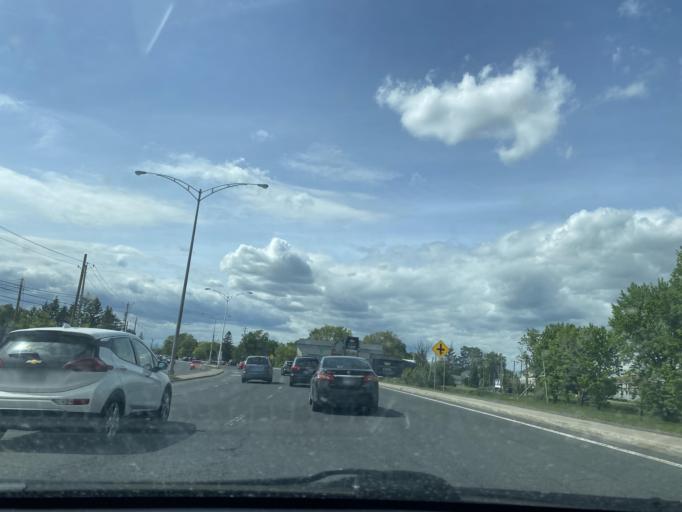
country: CA
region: Quebec
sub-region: Monteregie
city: Carignan
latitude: 45.4578
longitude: -73.3032
